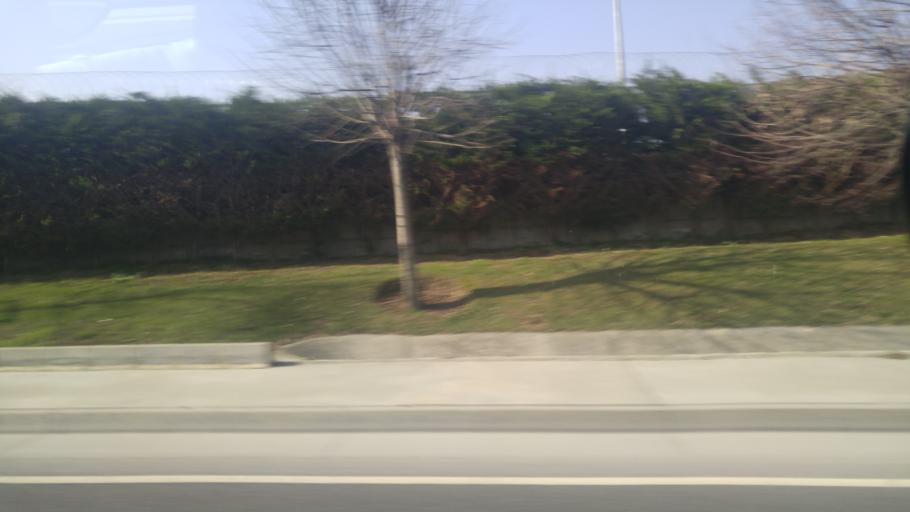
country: TR
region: Istanbul
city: Bahcelievler
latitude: 40.9788
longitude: 28.8406
